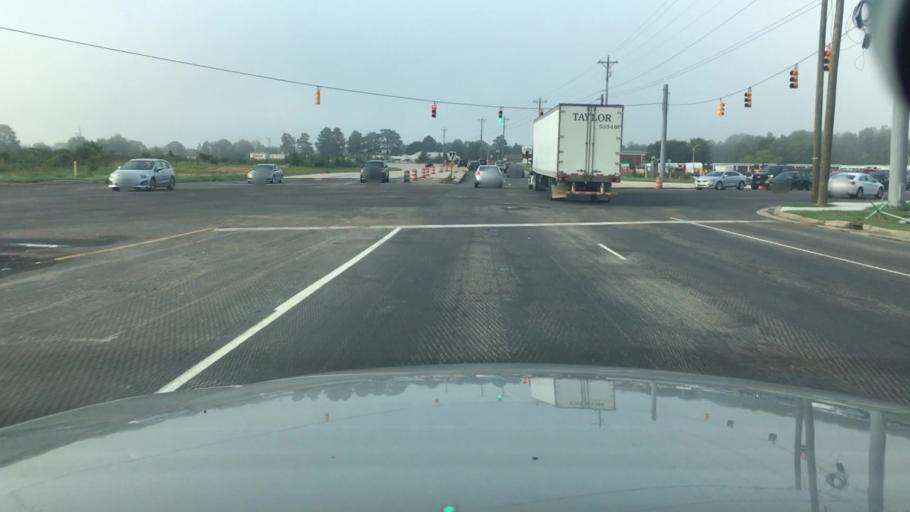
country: US
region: North Carolina
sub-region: Cumberland County
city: Hope Mills
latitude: 35.0083
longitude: -78.9188
